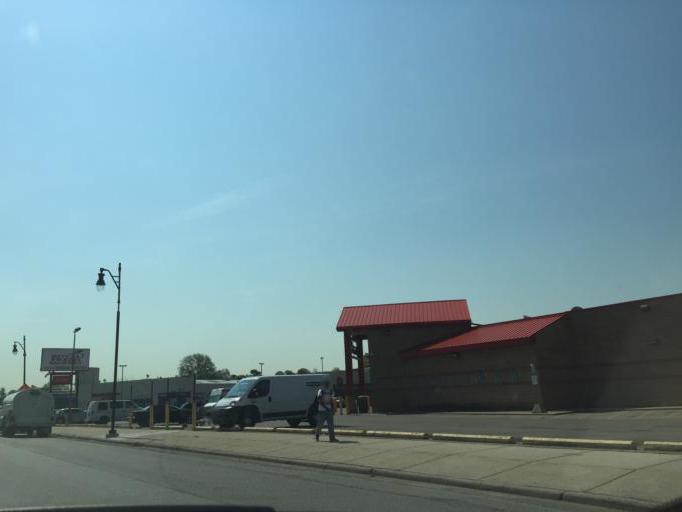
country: US
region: Michigan
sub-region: Oakland County
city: Oak Park
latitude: 42.4030
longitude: -83.2241
